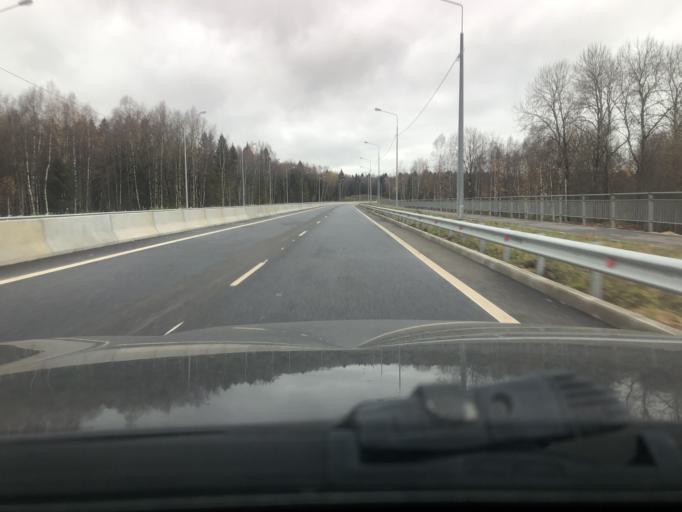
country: RU
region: Moskovskaya
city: Semkhoz
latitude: 56.3279
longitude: 38.0777
